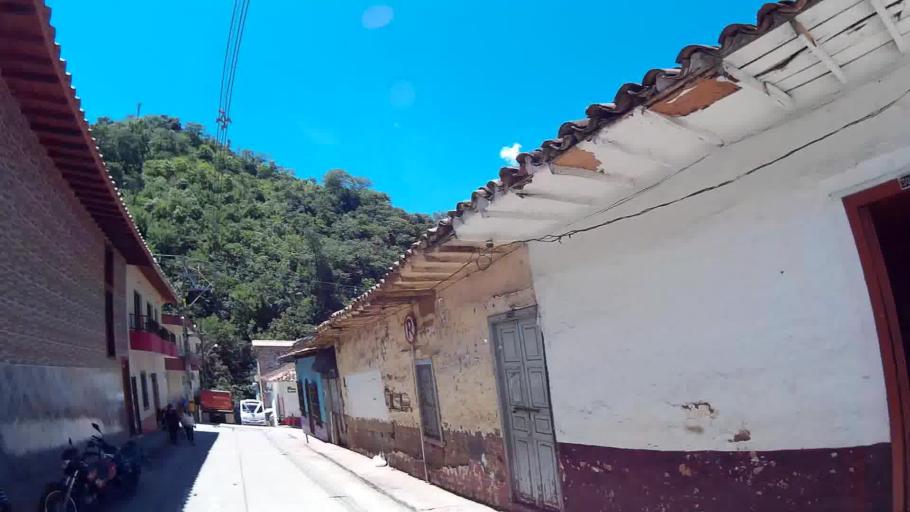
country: CO
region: Antioquia
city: Salgar
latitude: 5.9625
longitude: -75.9784
